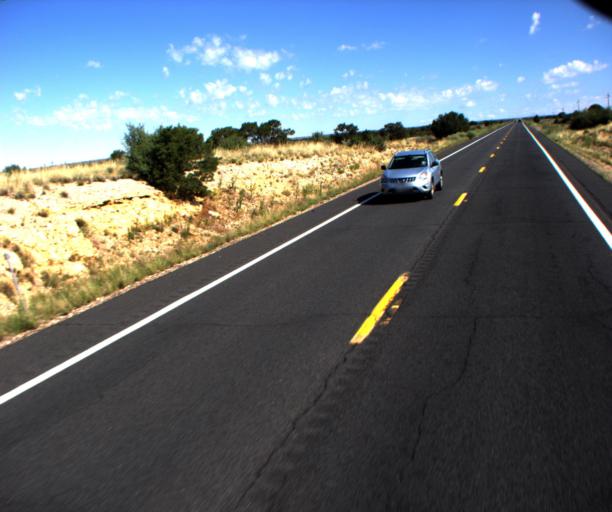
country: US
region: Arizona
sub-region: Coconino County
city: Grand Canyon Village
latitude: 35.7183
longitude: -112.1312
